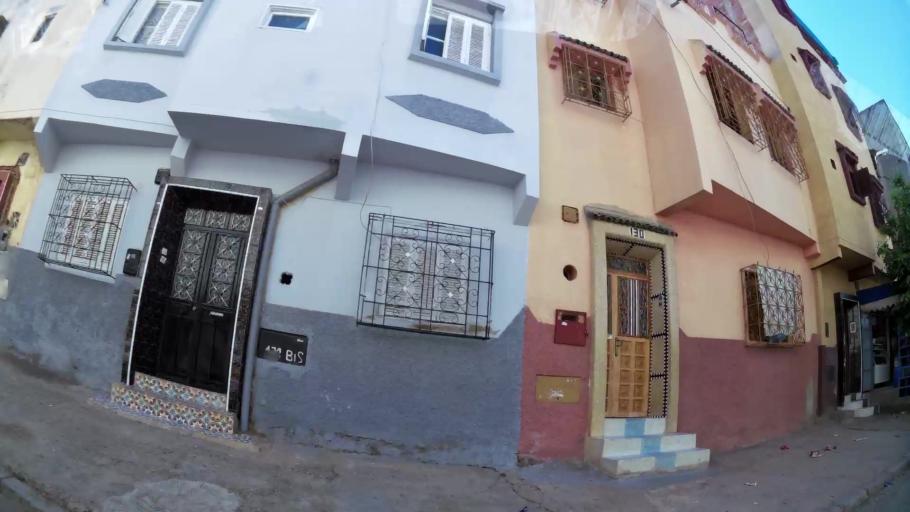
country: MA
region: Meknes-Tafilalet
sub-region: Meknes
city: Meknes
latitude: 33.9097
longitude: -5.5356
